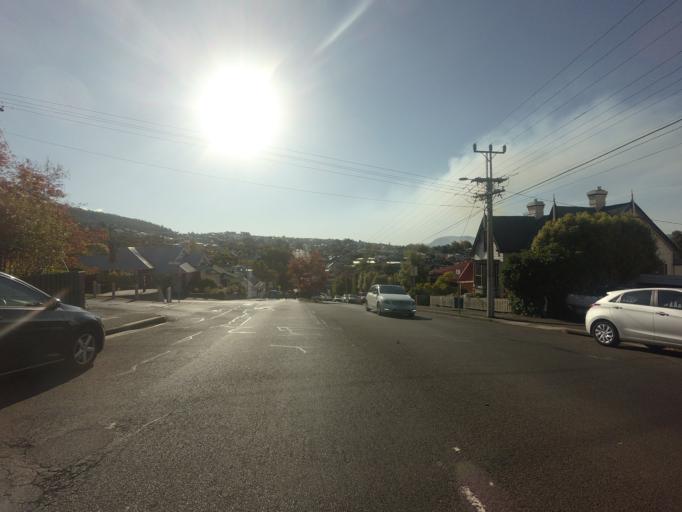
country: AU
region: Tasmania
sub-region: Hobart
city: Sandy Bay
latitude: -42.8829
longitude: 147.3142
